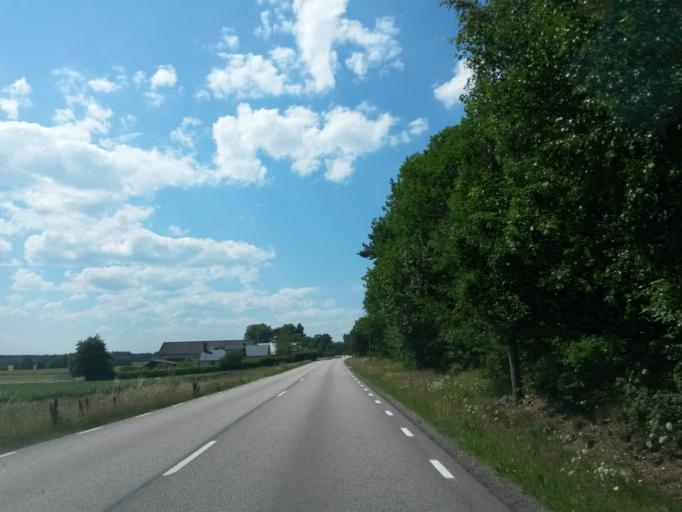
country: SE
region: Vaestra Goetaland
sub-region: Essunga Kommun
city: Nossebro
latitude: 58.1876
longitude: 12.7618
